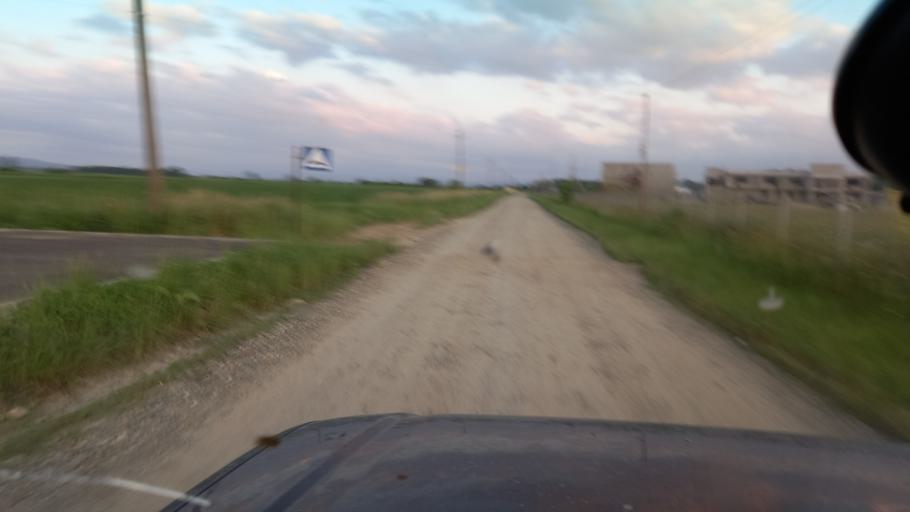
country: RU
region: Krasnodarskiy
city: Mostovskoy
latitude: 44.4368
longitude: 40.7424
